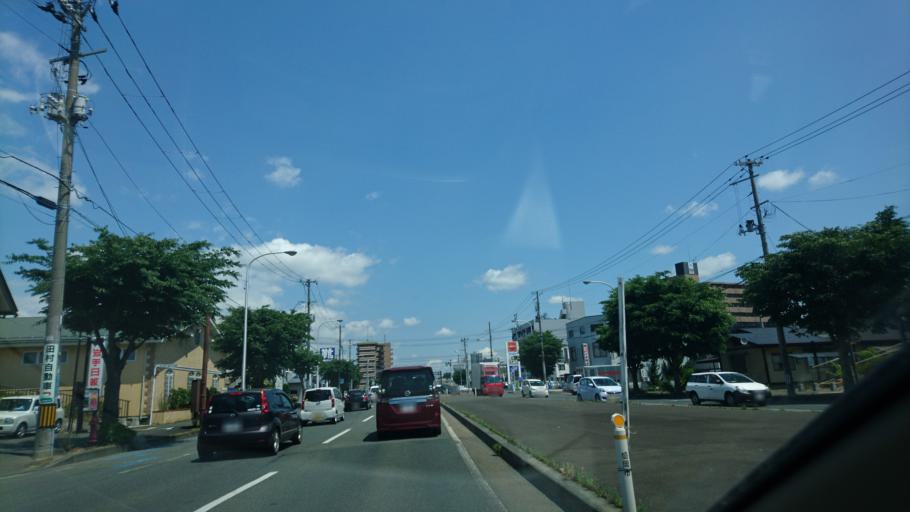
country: JP
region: Iwate
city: Morioka-shi
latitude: 39.6875
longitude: 141.1356
